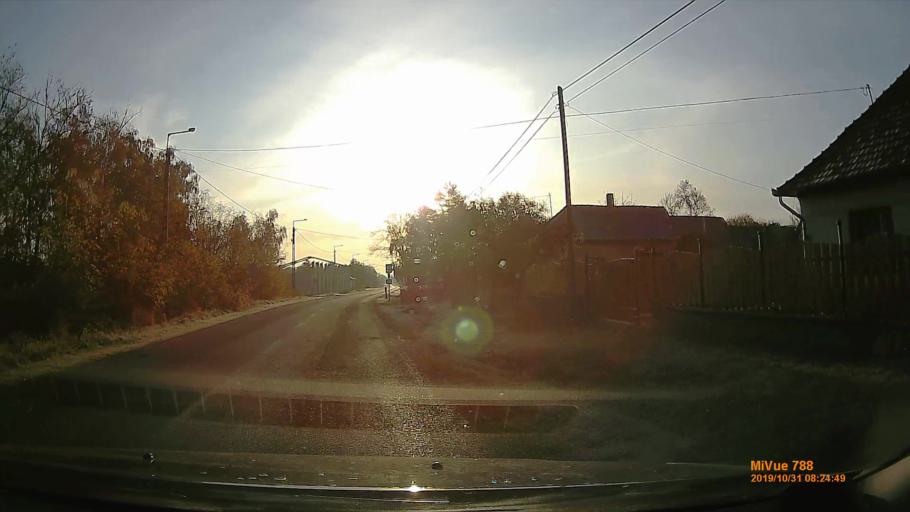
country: HU
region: Pest
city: Tapiobicske
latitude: 47.3682
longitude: 19.6630
